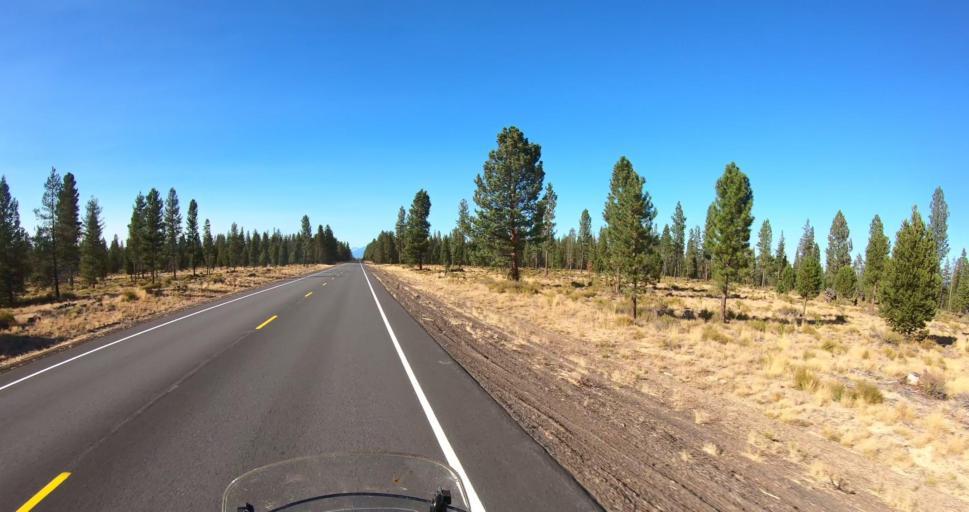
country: US
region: Oregon
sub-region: Deschutes County
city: La Pine
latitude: 43.5528
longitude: -121.4726
